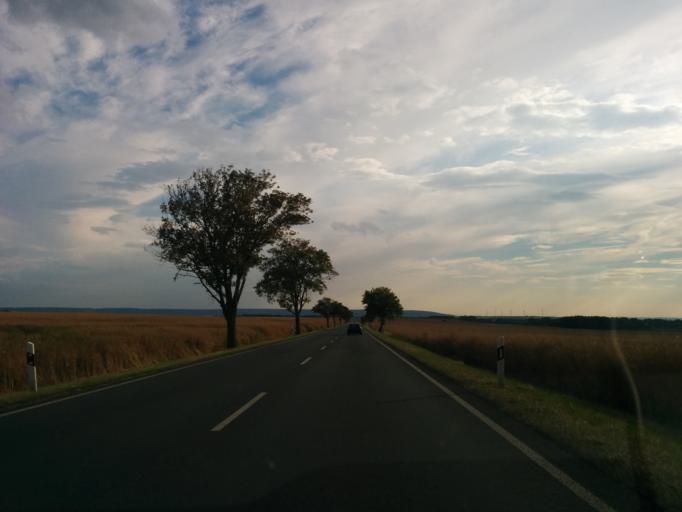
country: DE
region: Thuringia
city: Henschleben
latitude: 51.1384
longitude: 10.9653
